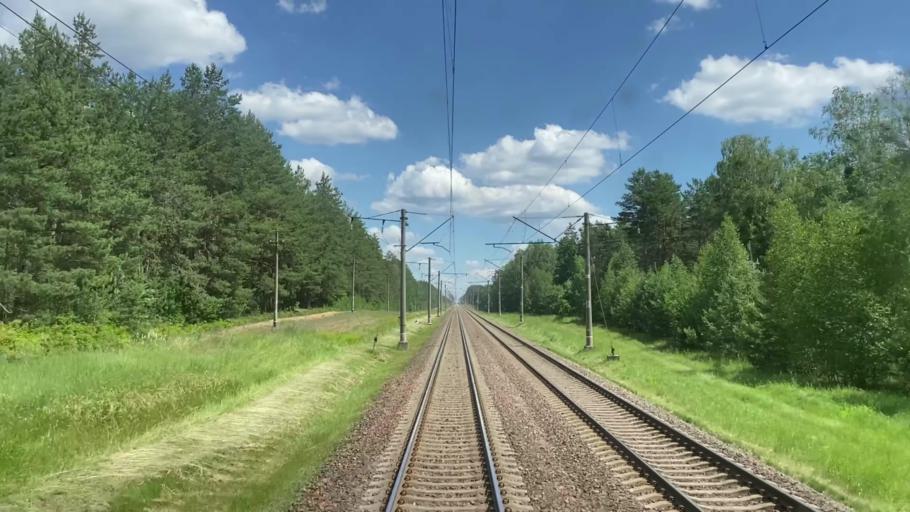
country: BY
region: Brest
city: Ivatsevichy
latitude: 52.8528
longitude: 25.5735
